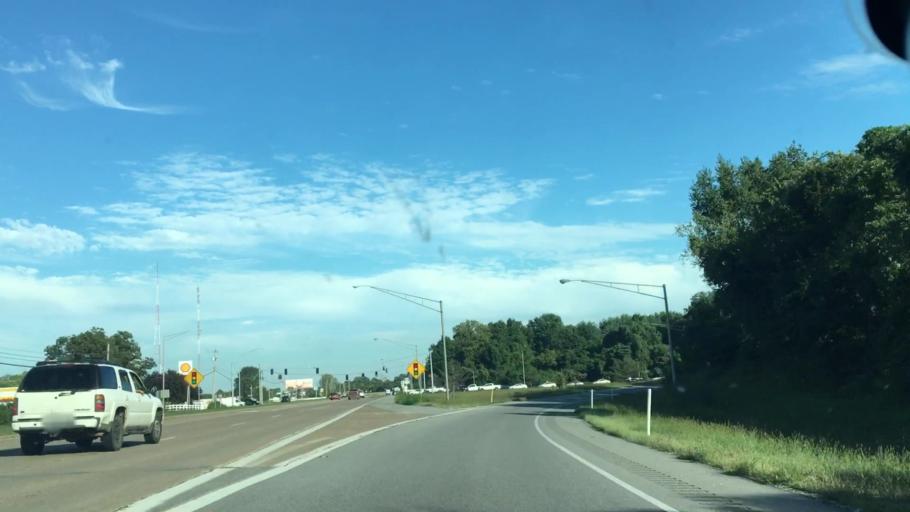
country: US
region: Kentucky
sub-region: Daviess County
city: Owensboro
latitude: 37.7756
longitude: -87.1680
